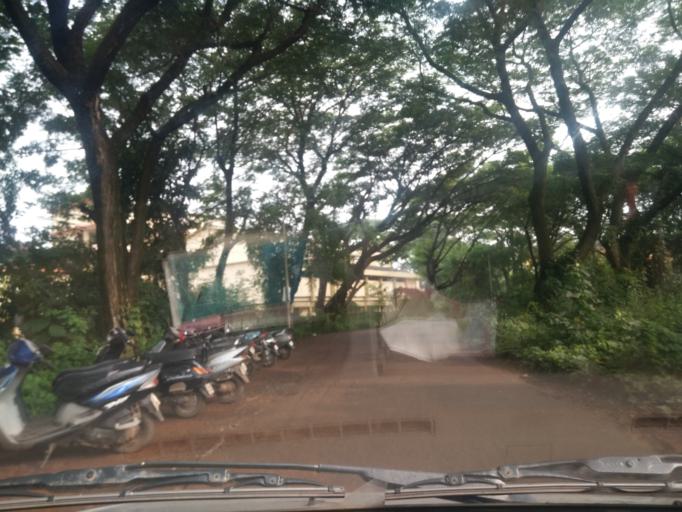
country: IN
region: Goa
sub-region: South Goa
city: Madgaon
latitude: 15.2740
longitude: 73.9523
